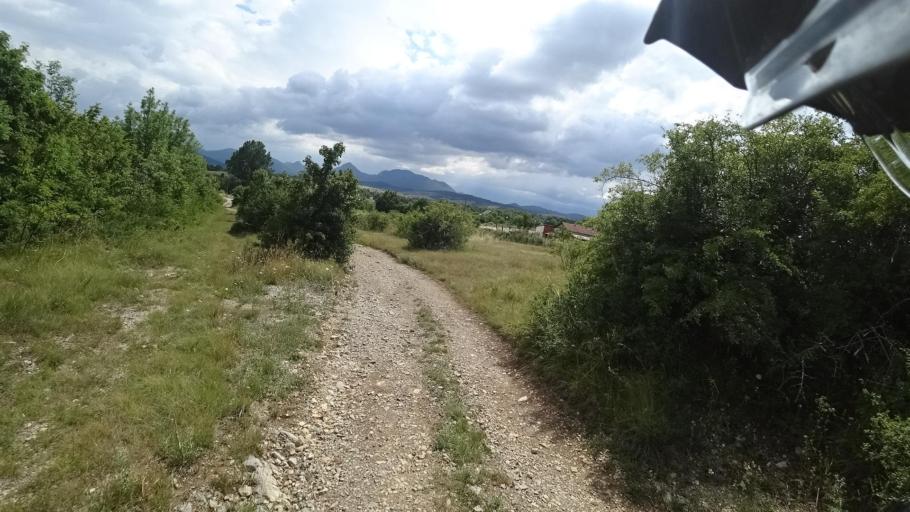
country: HR
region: Zadarska
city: Gracac
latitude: 44.5251
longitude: 15.7643
